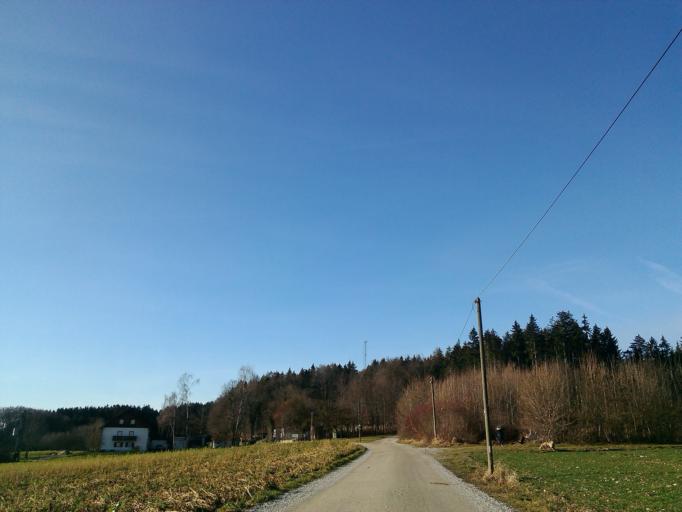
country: DE
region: Bavaria
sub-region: Upper Bavaria
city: Alling
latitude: 48.1425
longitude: 11.2842
